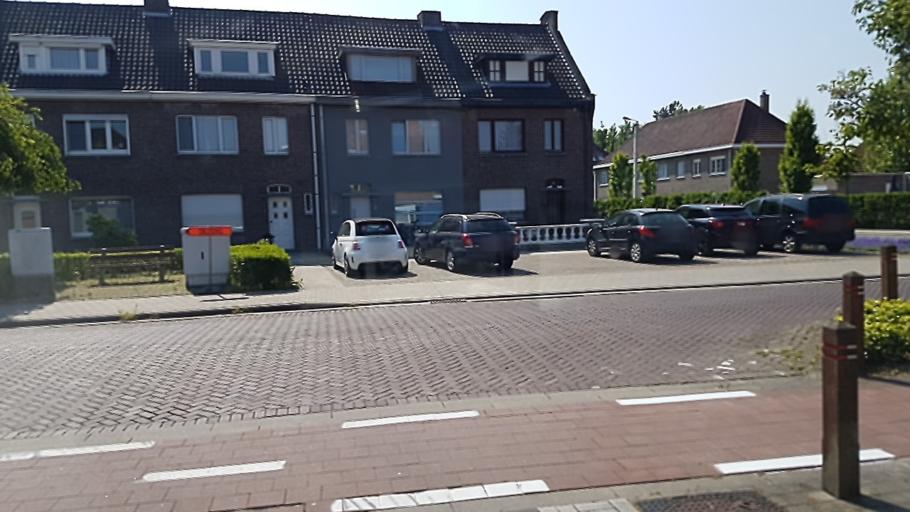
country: BE
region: Flanders
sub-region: Provincie West-Vlaanderen
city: Kuurne
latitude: 50.8399
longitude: 3.2933
